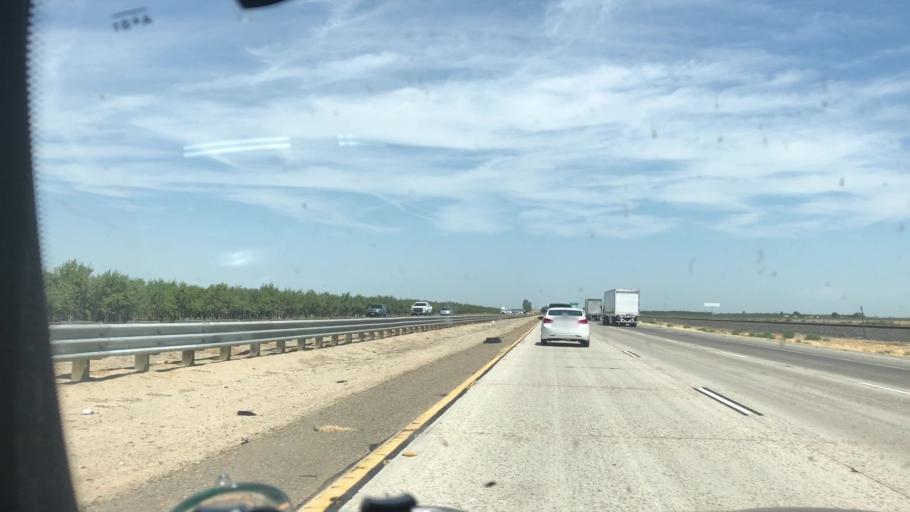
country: US
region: California
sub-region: Kern County
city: McFarland
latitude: 35.6311
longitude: -119.2161
